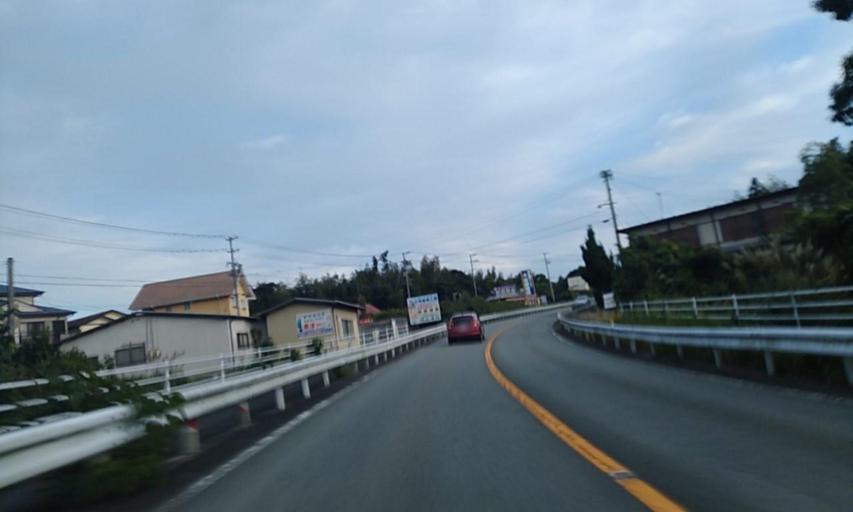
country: JP
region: Mie
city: Toba
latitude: 34.2950
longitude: 136.8797
